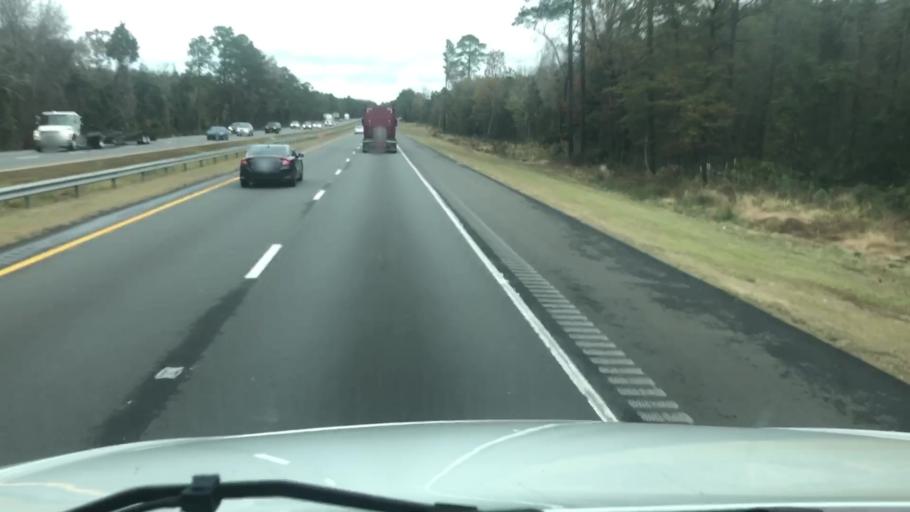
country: US
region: North Carolina
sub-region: Cumberland County
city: Eastover
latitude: 35.1040
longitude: -78.7716
